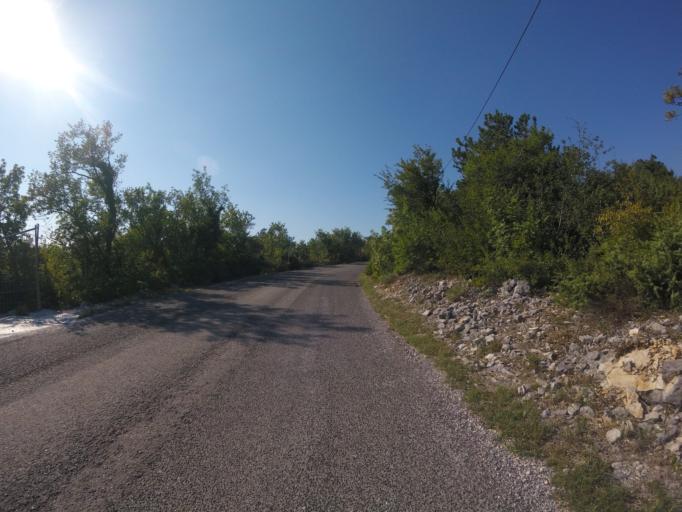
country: HR
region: Primorsko-Goranska
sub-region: Grad Crikvenica
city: Jadranovo
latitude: 45.2312
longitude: 14.6217
